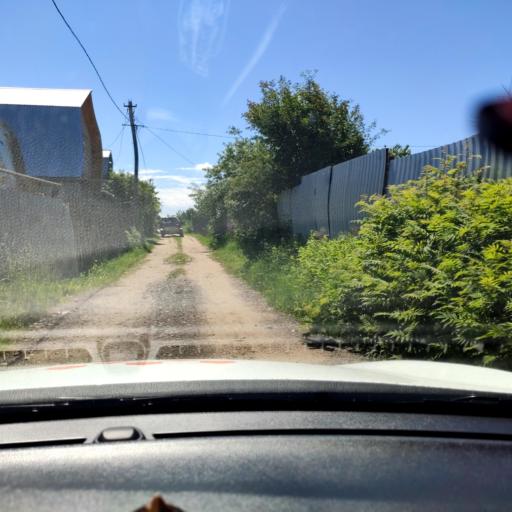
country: RU
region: Tatarstan
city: Stolbishchi
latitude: 55.6982
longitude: 49.1852
